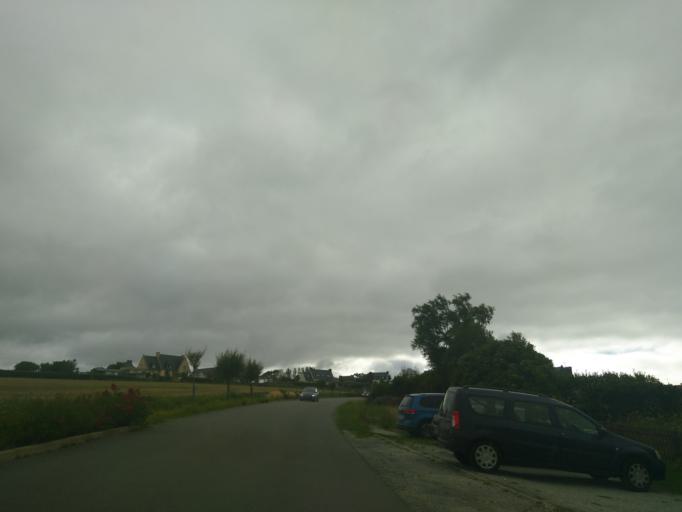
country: FR
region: Brittany
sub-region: Departement du Finistere
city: Plomodiern
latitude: 48.1730
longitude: -4.2852
